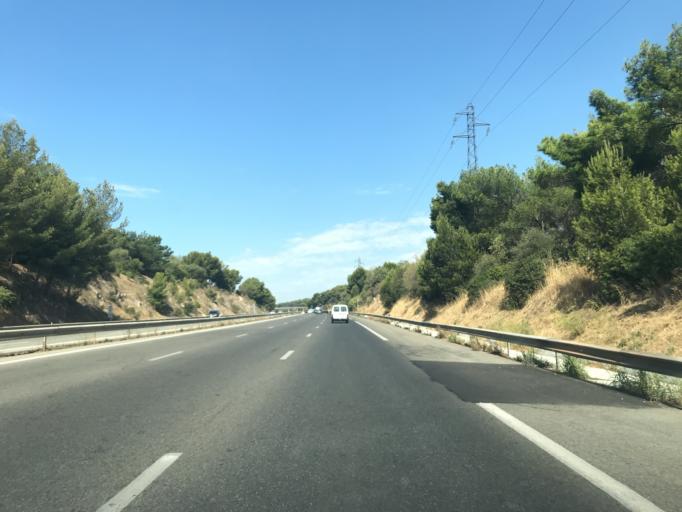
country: FR
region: Provence-Alpes-Cote d'Azur
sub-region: Departement du Var
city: Sanary-sur-Mer
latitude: 43.1365
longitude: 5.8065
